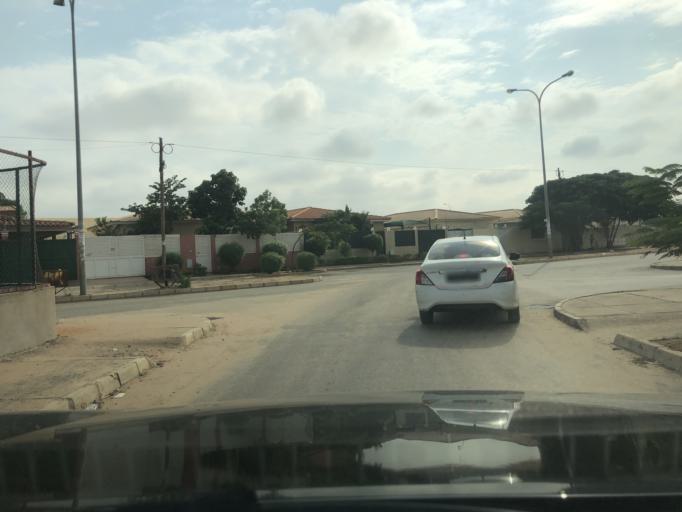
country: AO
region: Luanda
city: Luanda
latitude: -8.9352
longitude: 13.2469
